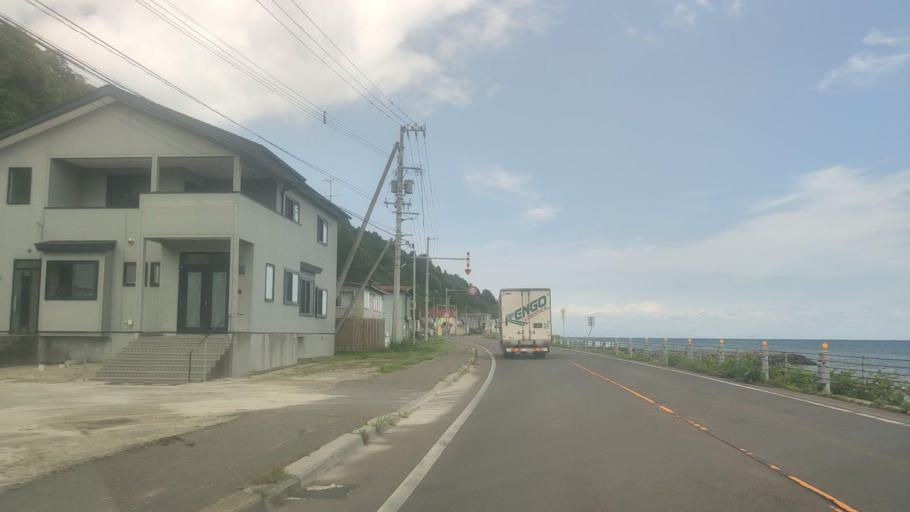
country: JP
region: Hokkaido
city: Nanae
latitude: 42.1398
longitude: 140.5042
